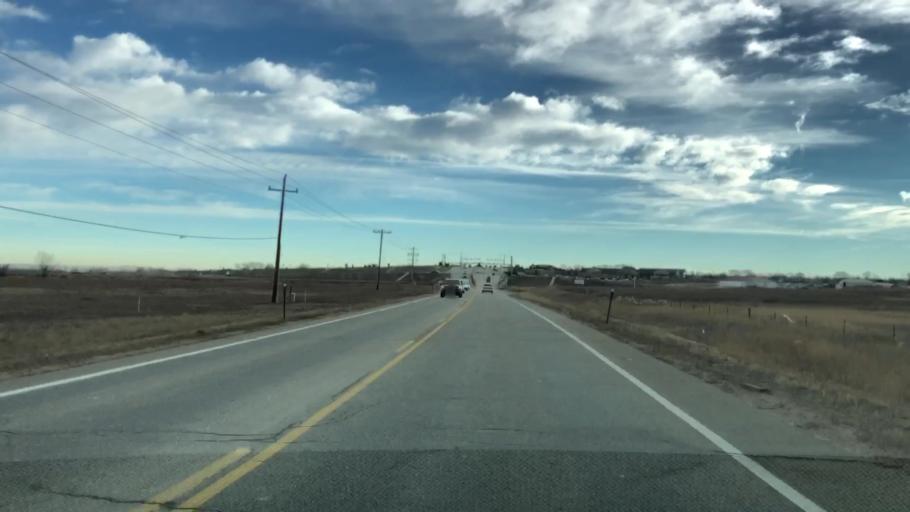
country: US
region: Colorado
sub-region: Weld County
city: Windsor
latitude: 40.4796
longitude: -105.0009
